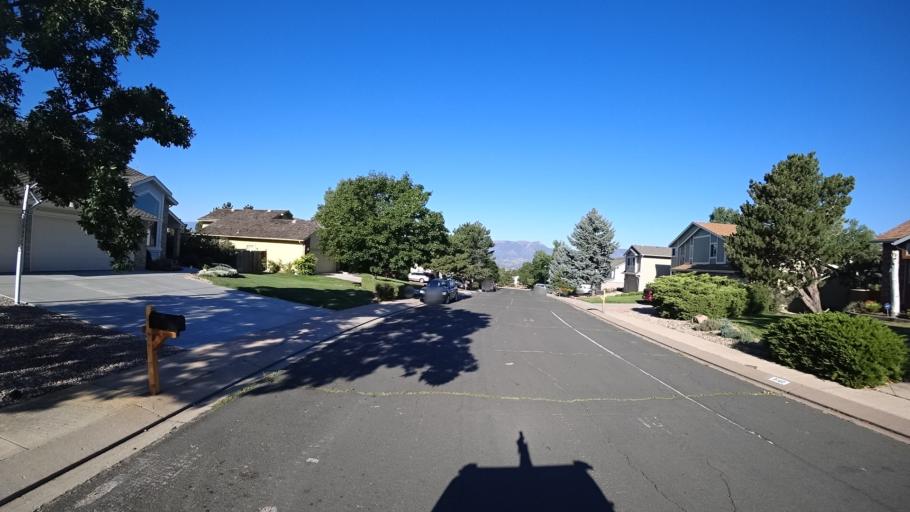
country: US
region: Colorado
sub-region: El Paso County
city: Black Forest
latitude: 38.9549
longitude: -104.7668
